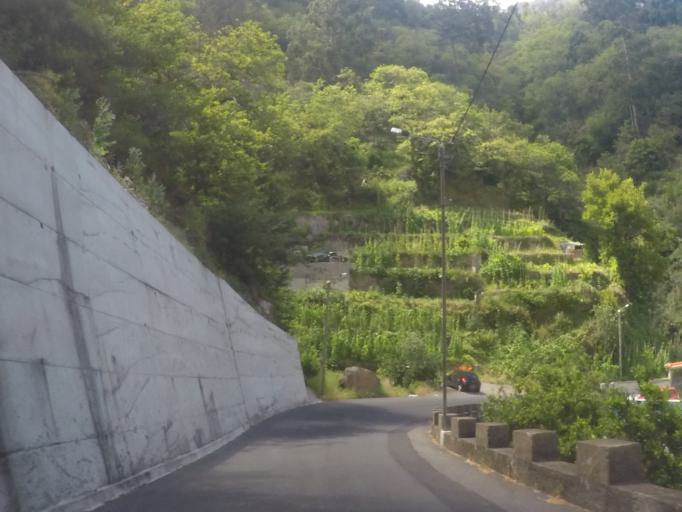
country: PT
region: Madeira
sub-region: Camara de Lobos
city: Curral das Freiras
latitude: 32.7108
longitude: -16.9734
